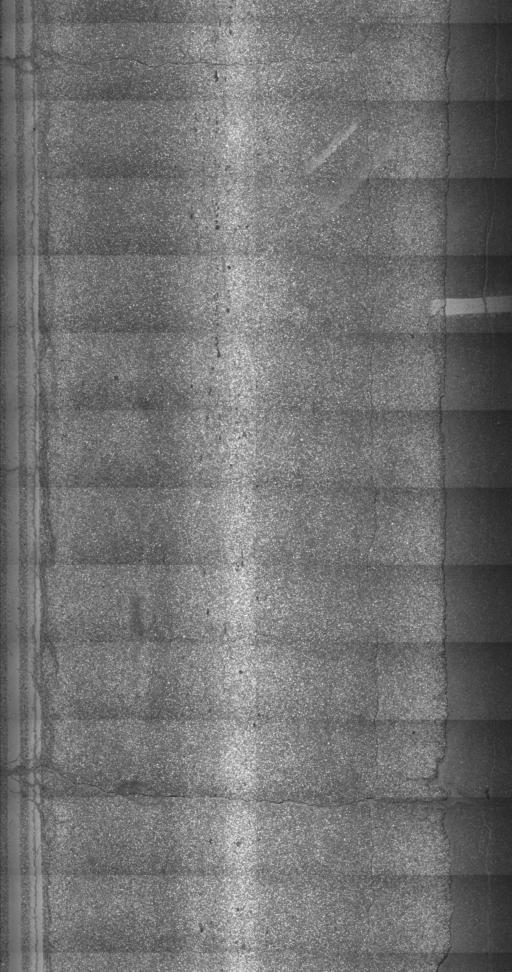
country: US
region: Vermont
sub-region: Washington County
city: Waterbury
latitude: 44.3331
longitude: -72.7516
